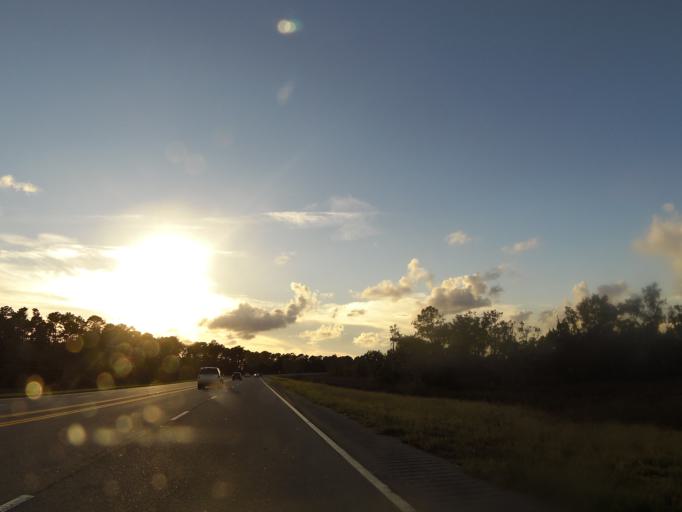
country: US
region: Georgia
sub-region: Glynn County
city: Brunswick
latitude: 31.1136
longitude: -81.5318
